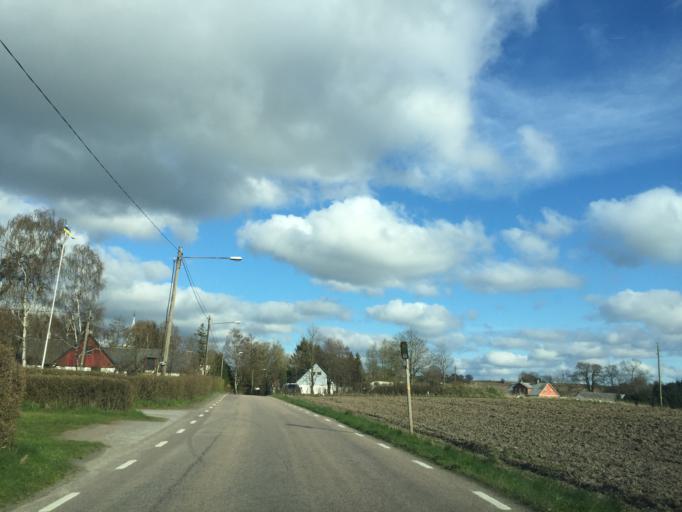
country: SE
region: Skane
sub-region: Skurups Kommun
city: Rydsgard
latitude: 55.4545
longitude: 13.6179
